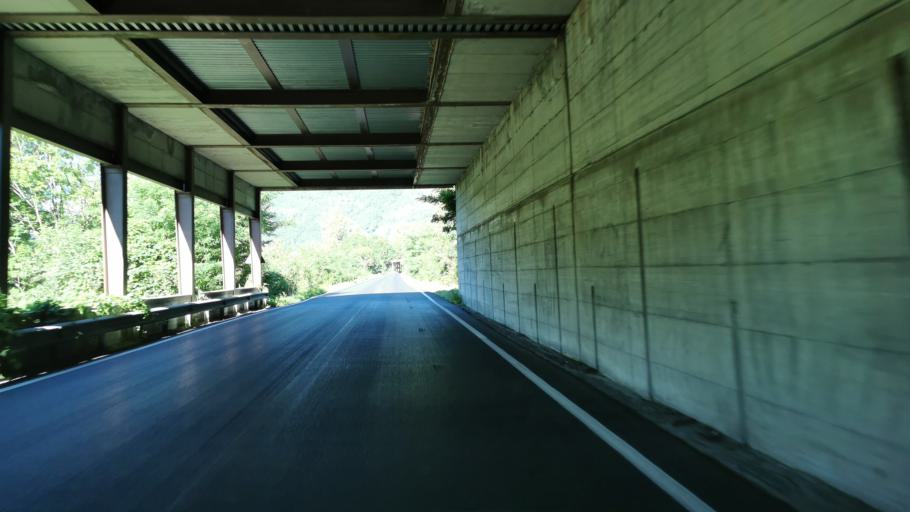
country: IT
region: Piedmont
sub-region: Provincia di Cuneo
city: Valdieri
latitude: 44.2616
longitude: 7.3692
